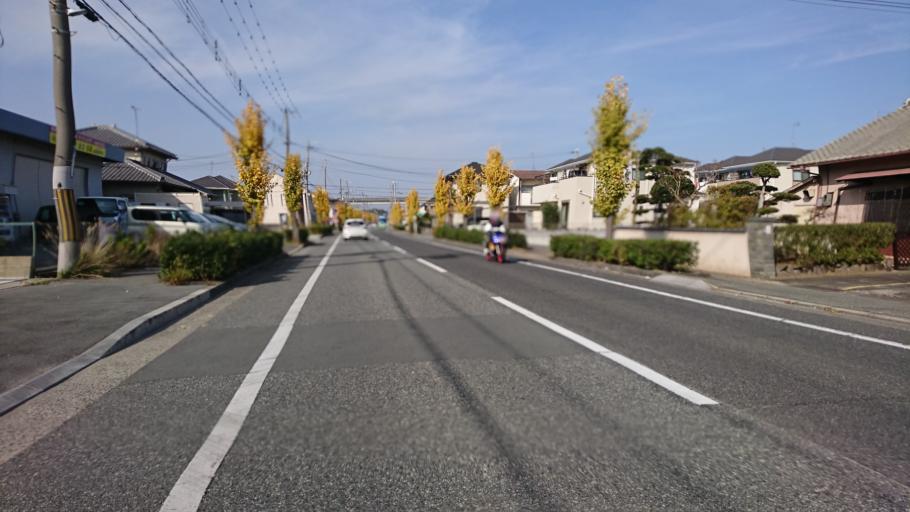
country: JP
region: Hyogo
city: Kakogawacho-honmachi
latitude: 34.7336
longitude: 134.8428
